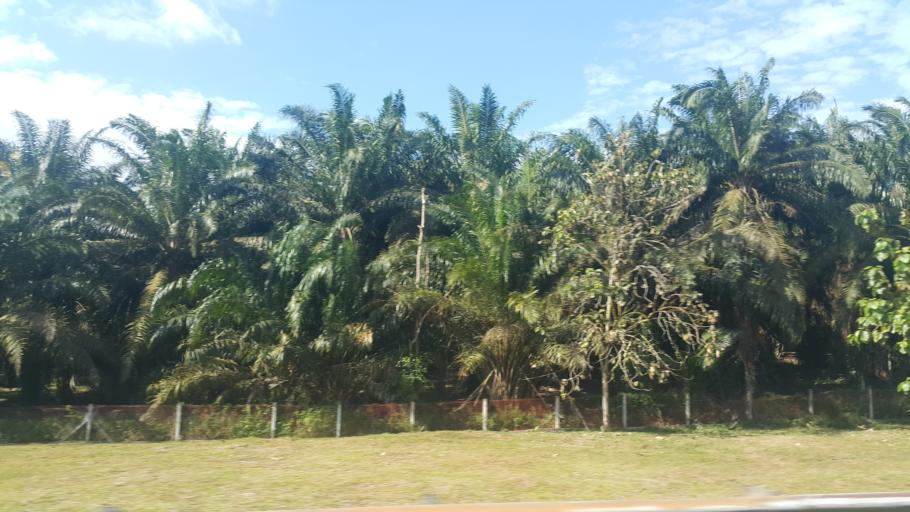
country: MY
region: Johor
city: Kelapa Sawit
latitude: 1.6731
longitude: 103.4856
